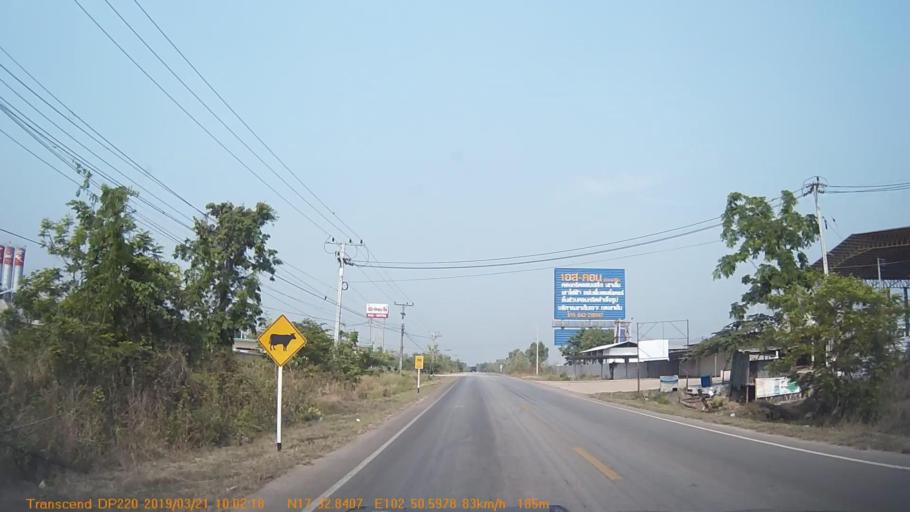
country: TH
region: Changwat Udon Thani
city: Udon Thani
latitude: 17.5474
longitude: 102.8430
